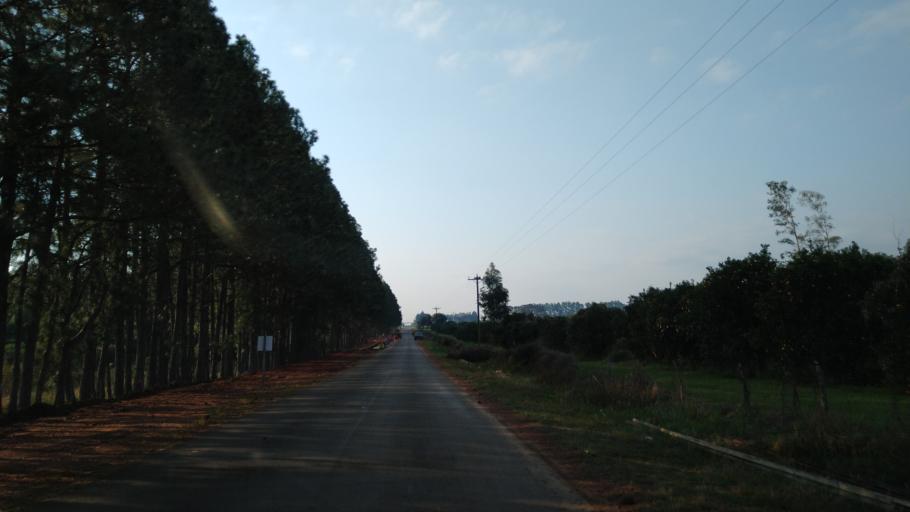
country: AR
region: Entre Rios
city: Santa Ana
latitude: -30.9083
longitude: -57.9259
